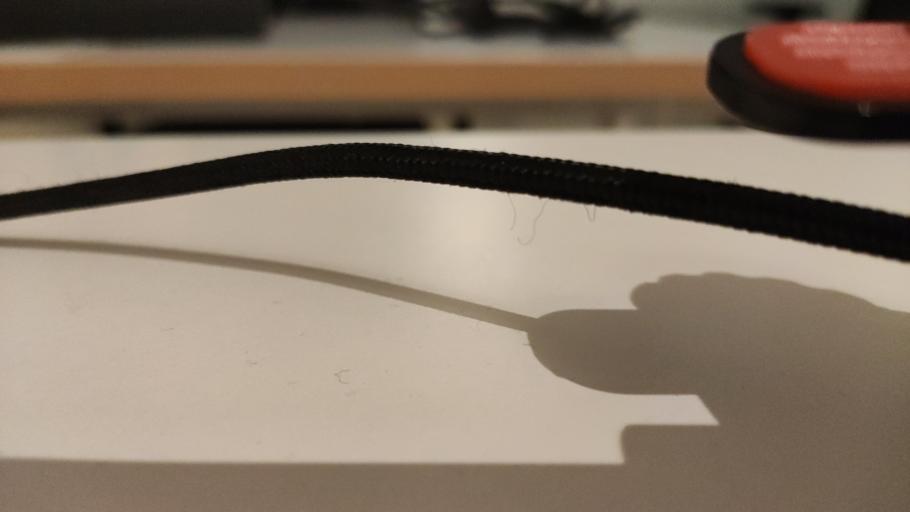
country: RU
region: Moskovskaya
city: Mikhnevo
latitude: 55.0798
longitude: 37.9599
